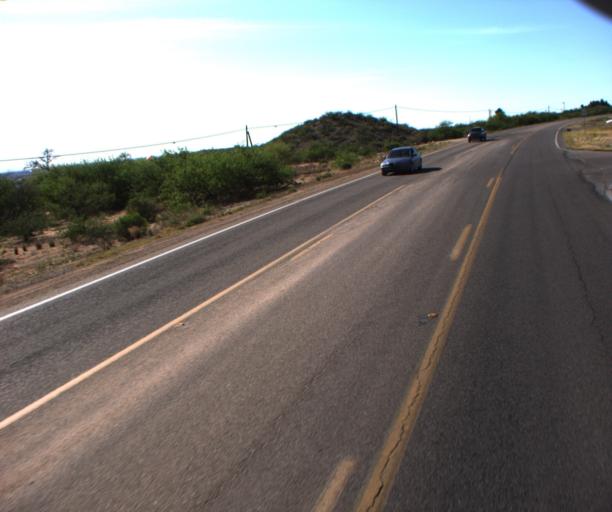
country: US
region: Arizona
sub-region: Cochise County
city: Benson
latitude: 31.9561
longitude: -110.2865
